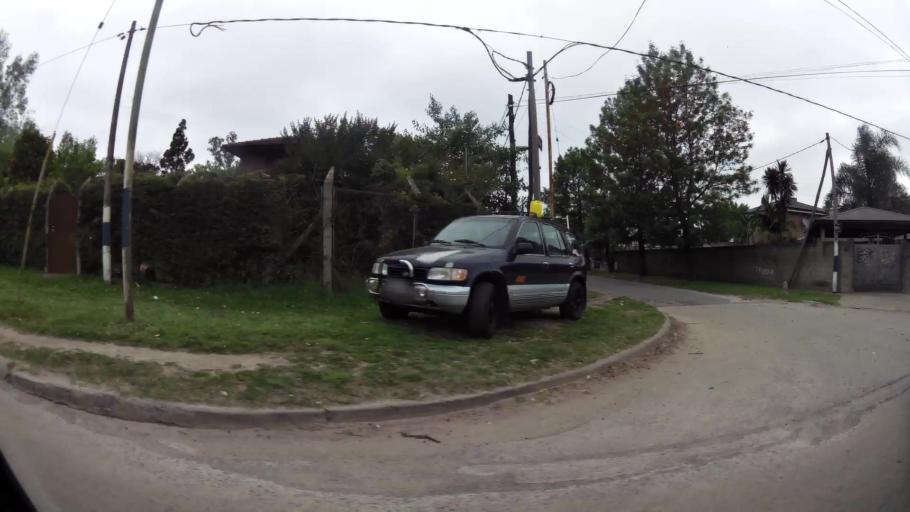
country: AR
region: Buenos Aires
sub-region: Partido de La Plata
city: La Plata
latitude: -34.9649
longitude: -58.0146
